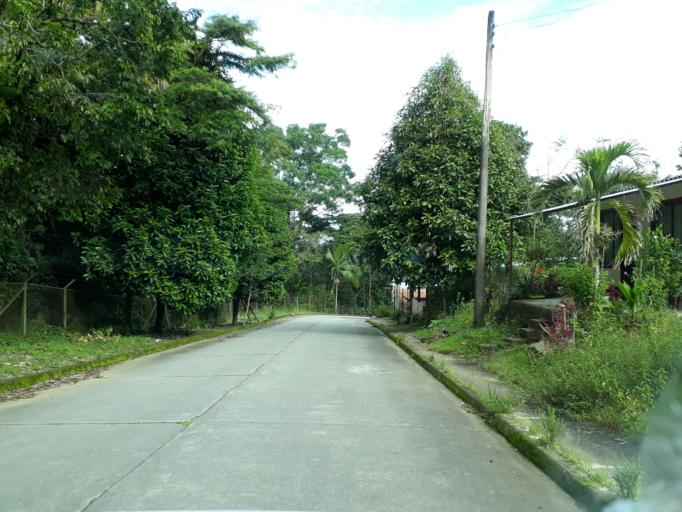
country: CO
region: Boyaca
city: Santa Maria
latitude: 4.7629
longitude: -73.3230
